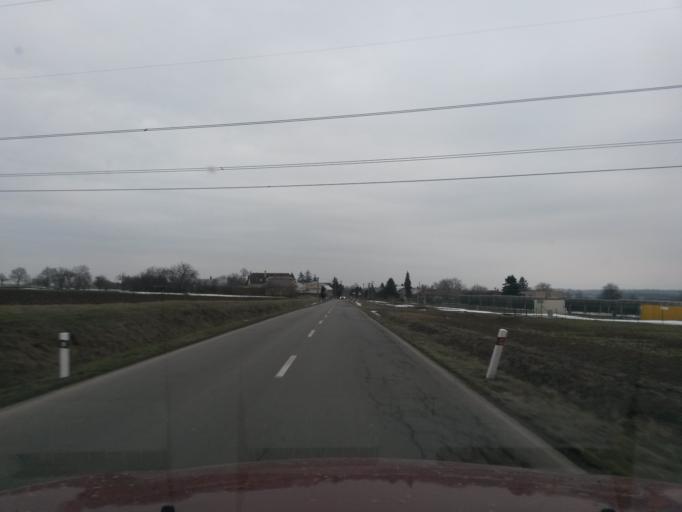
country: SK
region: Kosicky
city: Trebisov
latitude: 48.6907
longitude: 21.8100
